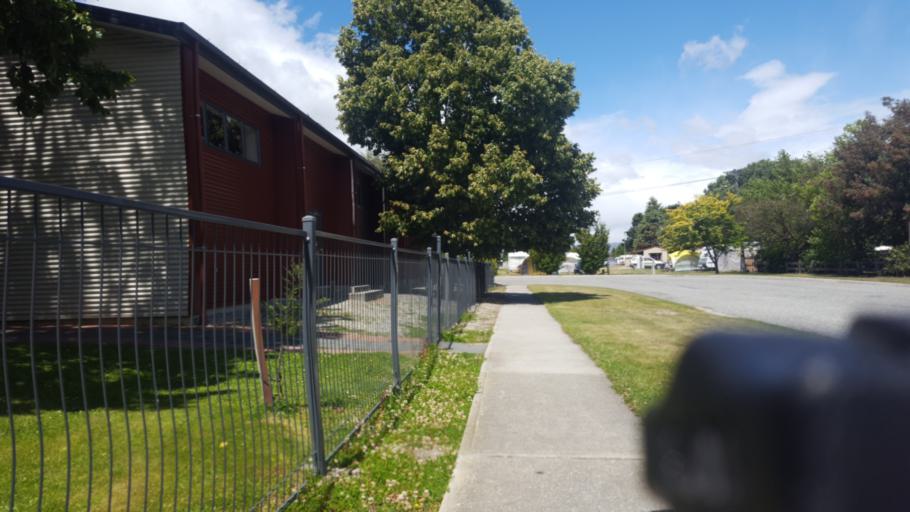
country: NZ
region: Otago
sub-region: Queenstown-Lakes District
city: Wanaka
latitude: -45.1917
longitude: 169.3186
